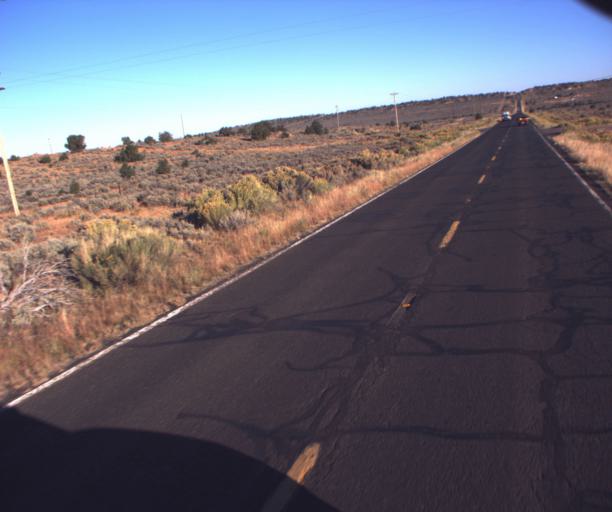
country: US
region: Arizona
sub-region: Apache County
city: Ganado
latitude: 35.5968
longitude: -109.5389
